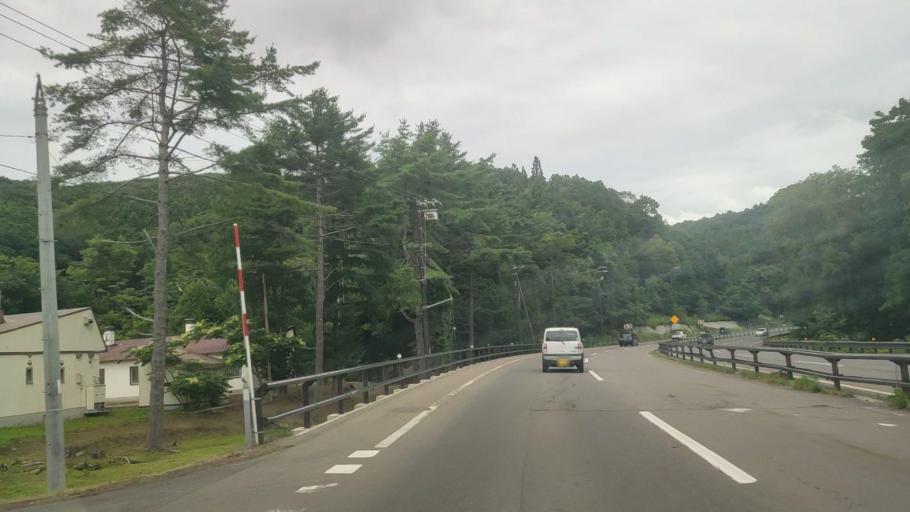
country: JP
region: Hokkaido
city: Nanae
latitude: 41.9616
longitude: 140.6472
